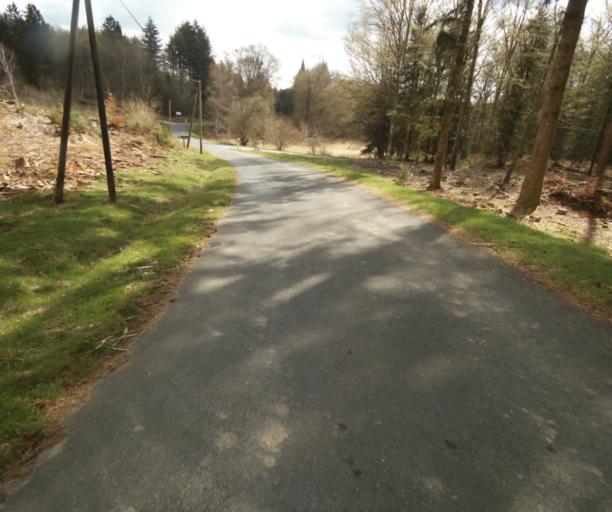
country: FR
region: Limousin
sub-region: Departement de la Correze
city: Argentat
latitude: 45.2424
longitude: 1.9563
